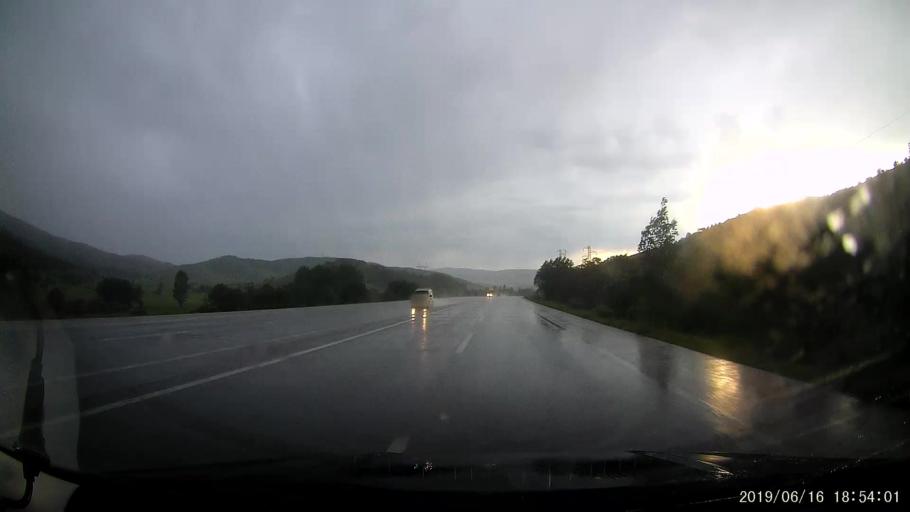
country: TR
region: Erzincan
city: Catalcam
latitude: 39.8965
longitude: 38.8634
